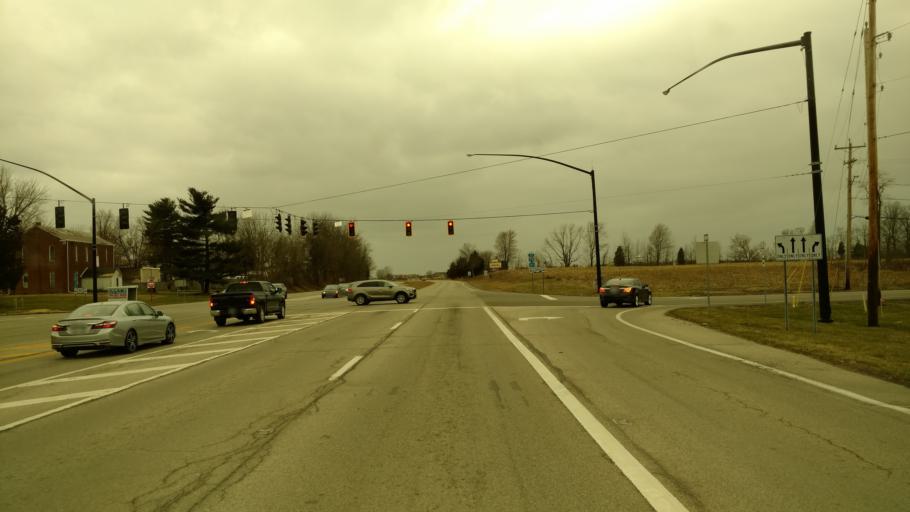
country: US
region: Ohio
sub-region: Licking County
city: Etna
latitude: 39.9591
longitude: -82.6820
